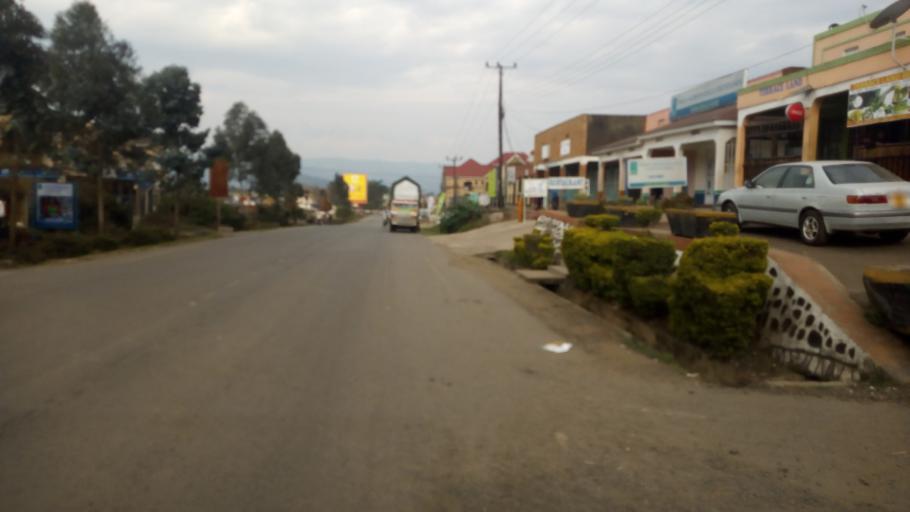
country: UG
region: Western Region
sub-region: Kisoro District
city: Kisoro
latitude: -1.2826
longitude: 29.6933
